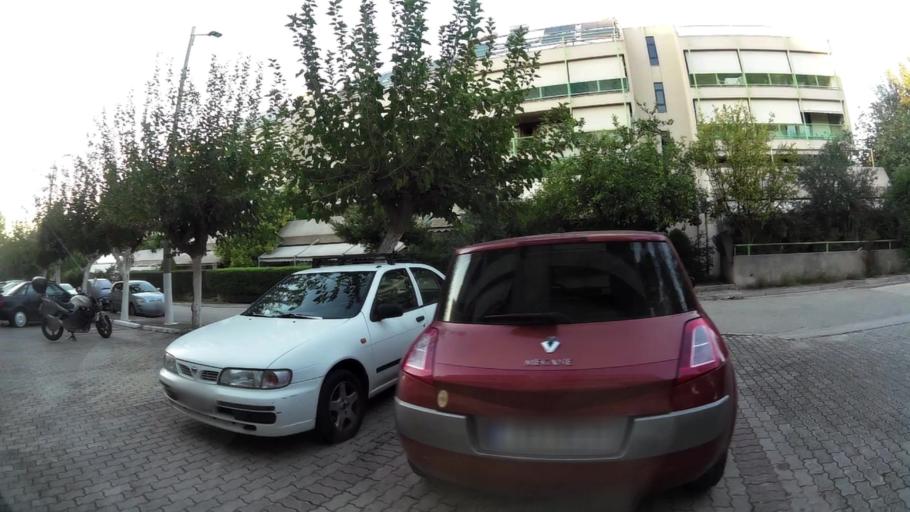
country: GR
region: Attica
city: Pefki
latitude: 38.0673
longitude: 23.7926
